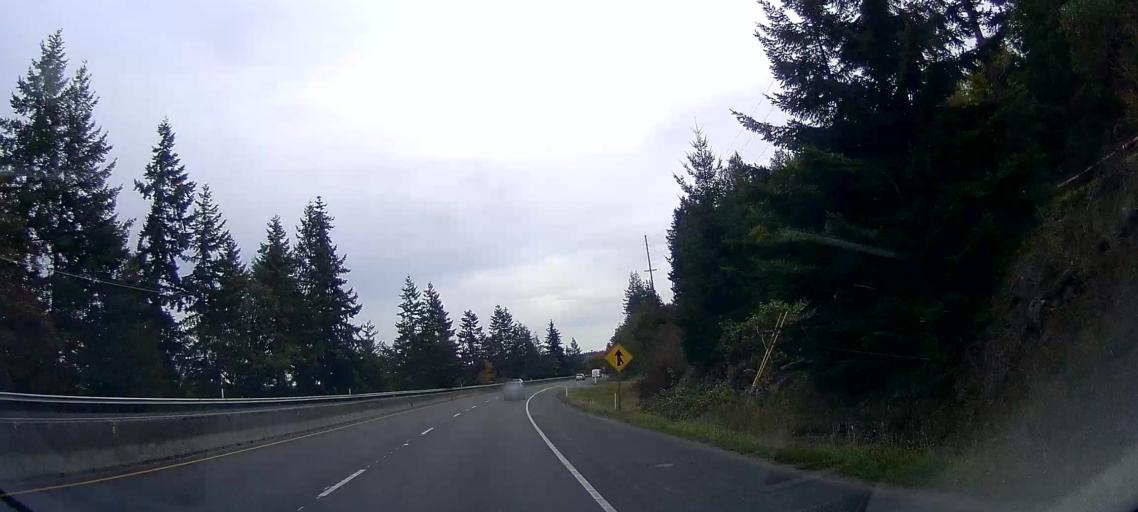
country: US
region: Washington
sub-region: Skagit County
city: Anacortes
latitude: 48.4758
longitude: -122.5903
